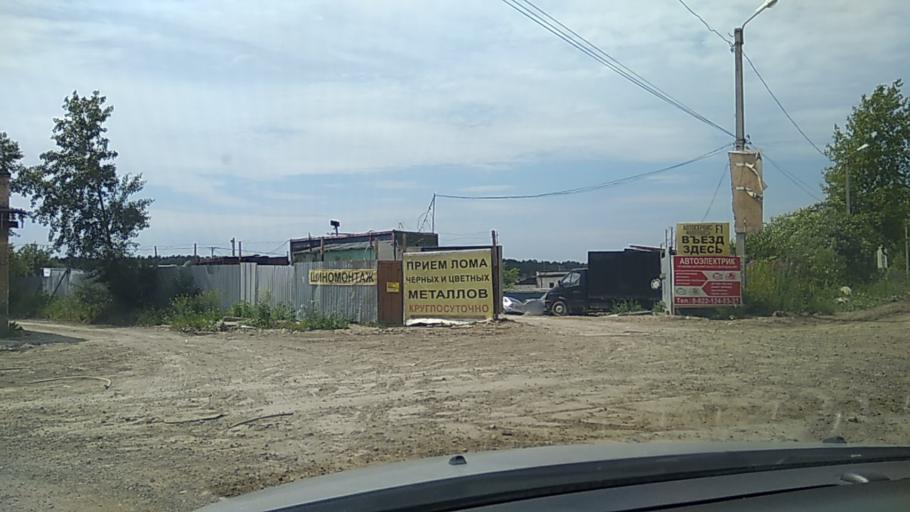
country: RU
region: Sverdlovsk
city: Verkhnyaya Pyshma
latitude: 56.9154
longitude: 60.5773
